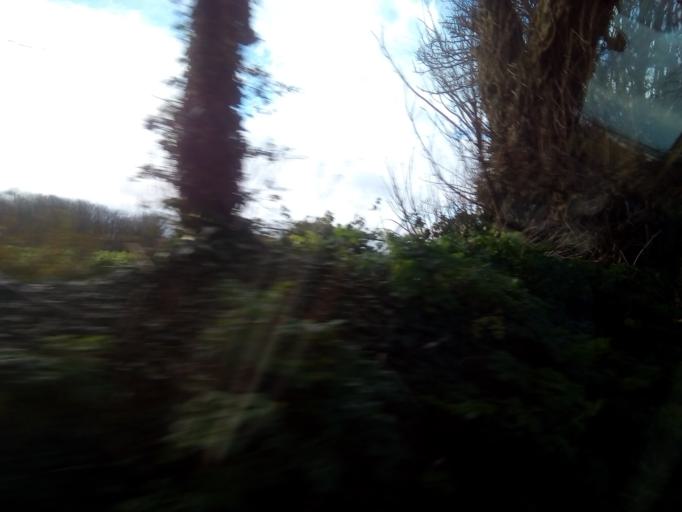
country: IE
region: Leinster
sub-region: Fingal County
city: Skerries
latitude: 53.5720
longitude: -6.1323
